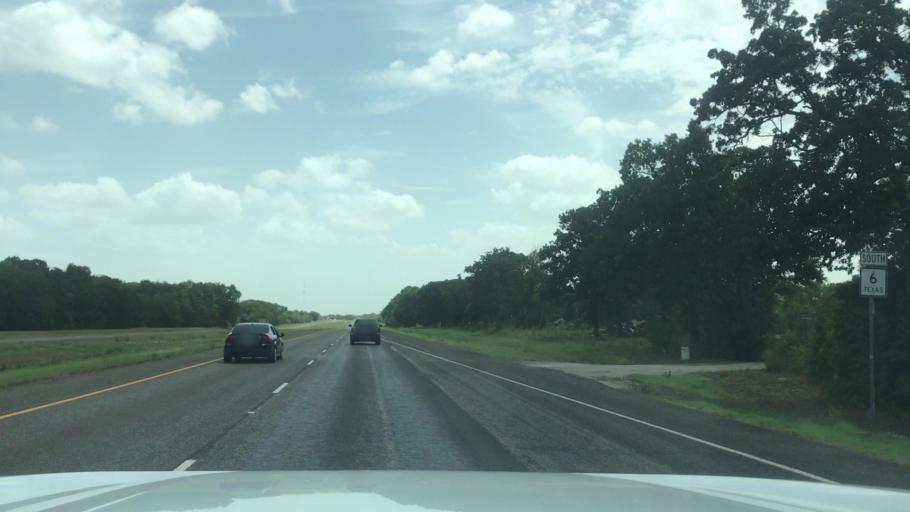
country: US
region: Texas
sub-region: Falls County
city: Marlin
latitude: 31.2938
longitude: -96.8751
